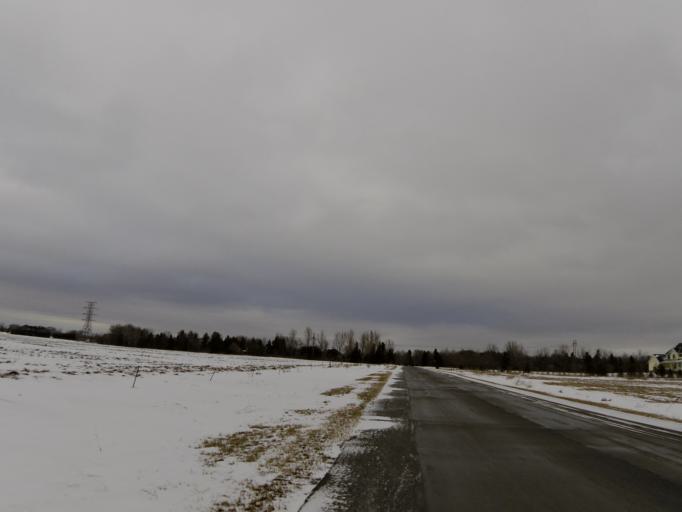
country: US
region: Minnesota
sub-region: Washington County
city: Lake Elmo
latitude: 44.9536
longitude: -92.8503
